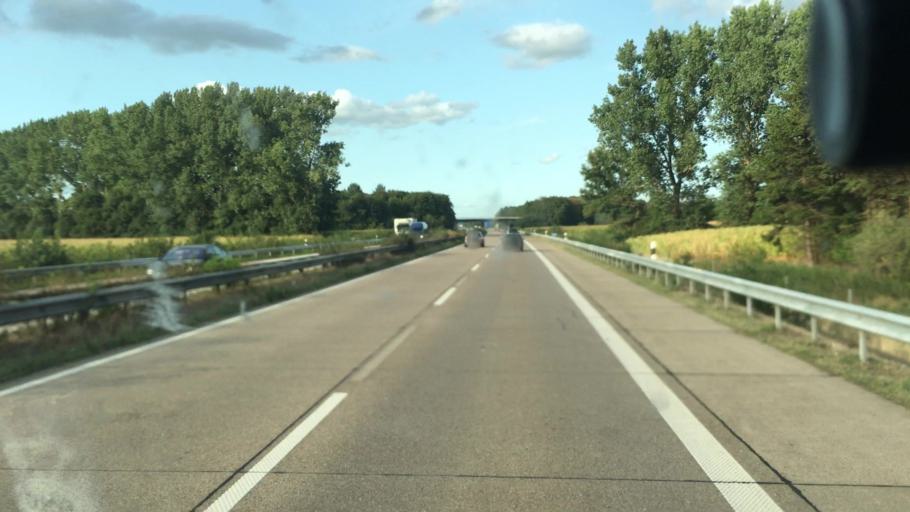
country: DE
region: Lower Saxony
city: Wardenburg
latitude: 53.0902
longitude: 8.2611
